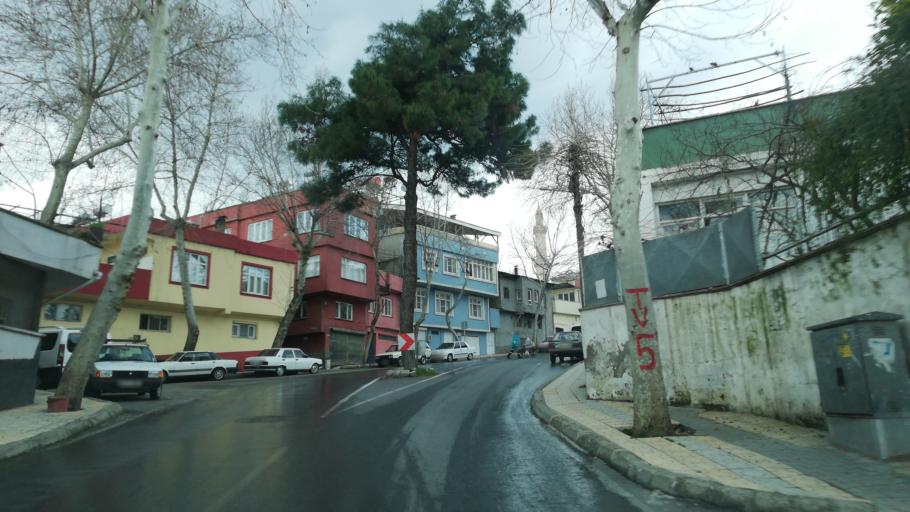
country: TR
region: Kahramanmaras
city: Kahramanmaras
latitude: 37.5844
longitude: 36.9332
